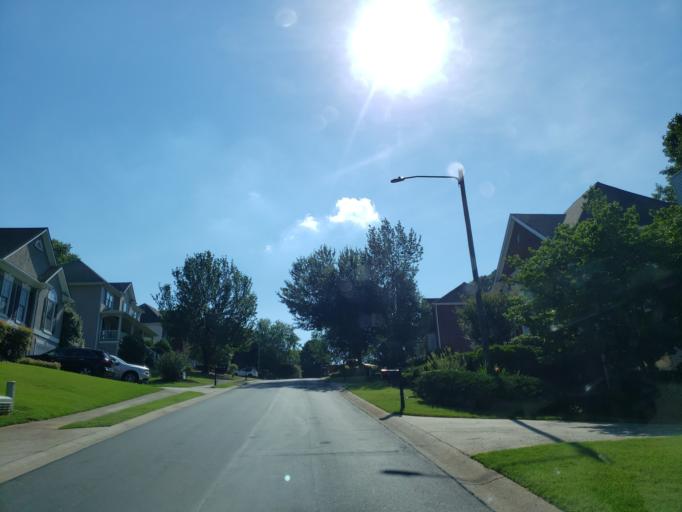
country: US
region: Georgia
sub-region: Cherokee County
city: Woodstock
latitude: 34.1207
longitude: -84.5332
